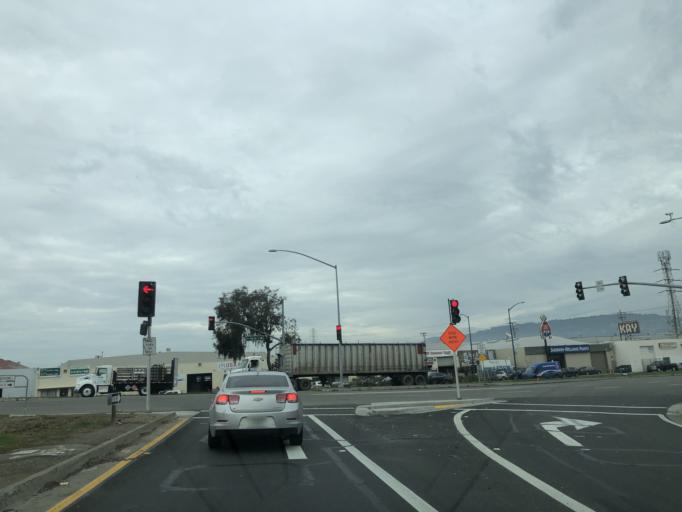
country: US
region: California
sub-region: Alameda County
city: Alameda
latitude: 37.7542
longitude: -122.2066
